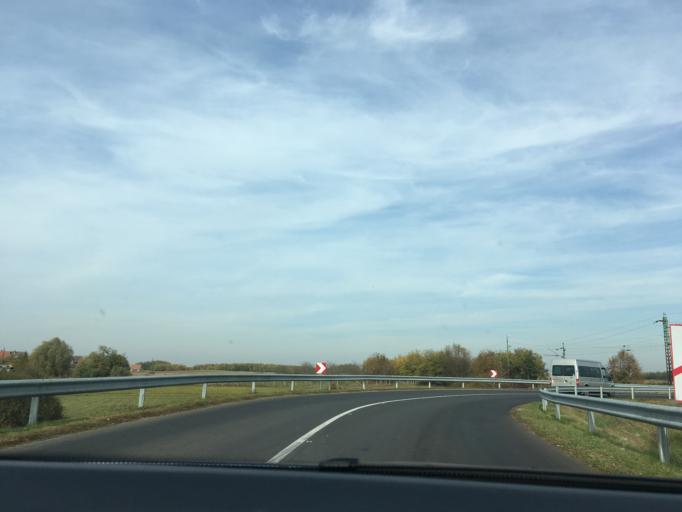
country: HU
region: Szabolcs-Szatmar-Bereg
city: Ujfeherto
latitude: 47.8181
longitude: 21.7056
